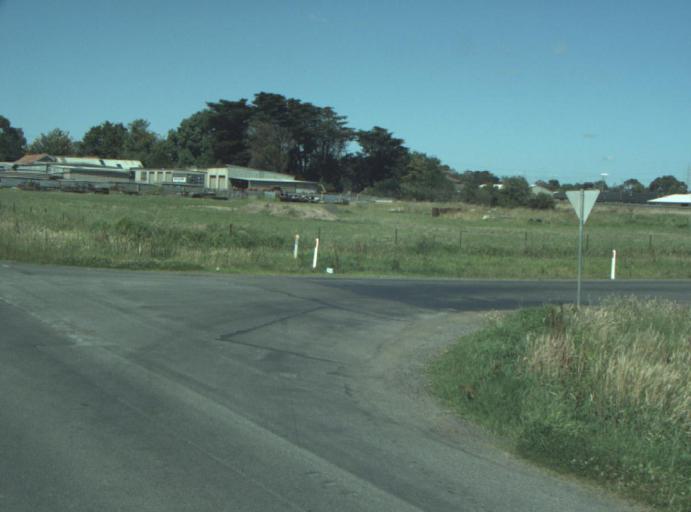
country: AU
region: Victoria
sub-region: Greater Geelong
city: Breakwater
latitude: -38.1946
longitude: 144.3530
